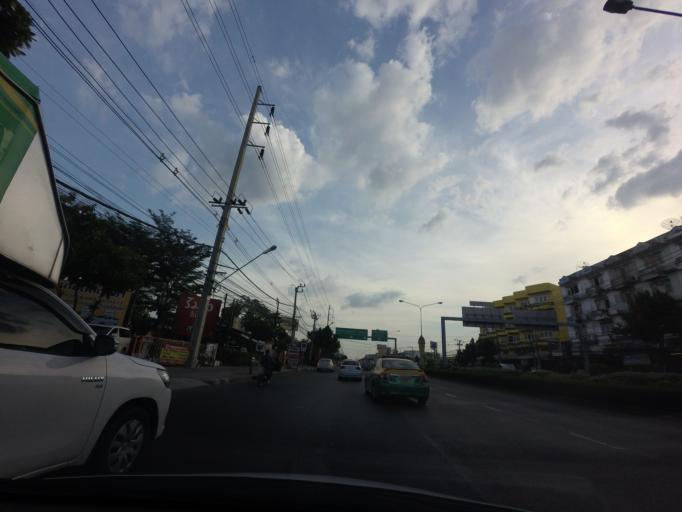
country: TH
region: Bangkok
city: Bang Khun Thian
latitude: 13.6523
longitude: 100.4308
